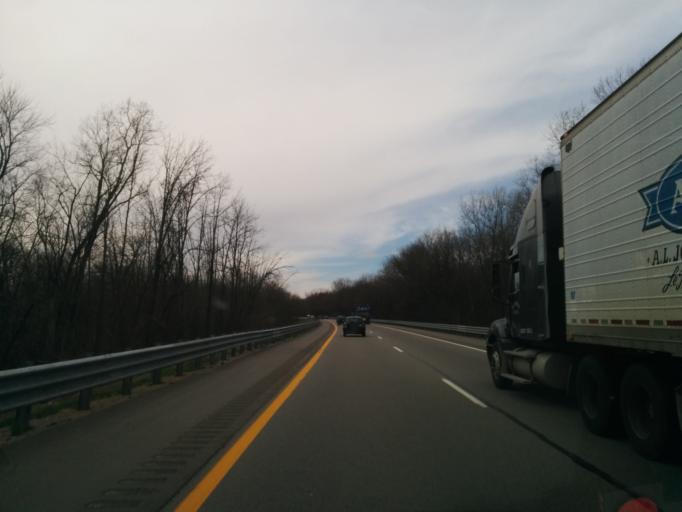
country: US
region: Michigan
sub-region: Kent County
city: Wyoming
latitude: 42.9325
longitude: -85.7315
